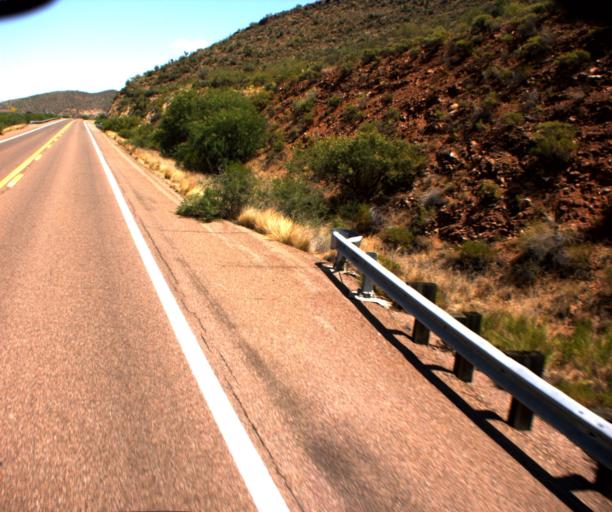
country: US
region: Arizona
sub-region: Gila County
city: Tonto Basin
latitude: 33.6836
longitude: -111.1705
